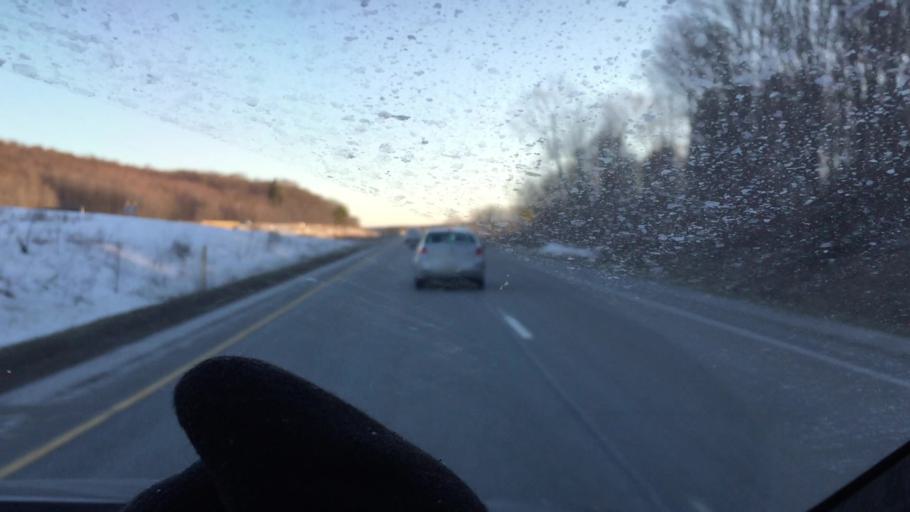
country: US
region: Pennsylvania
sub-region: Crawford County
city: Meadville
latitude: 41.6851
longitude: -80.2065
